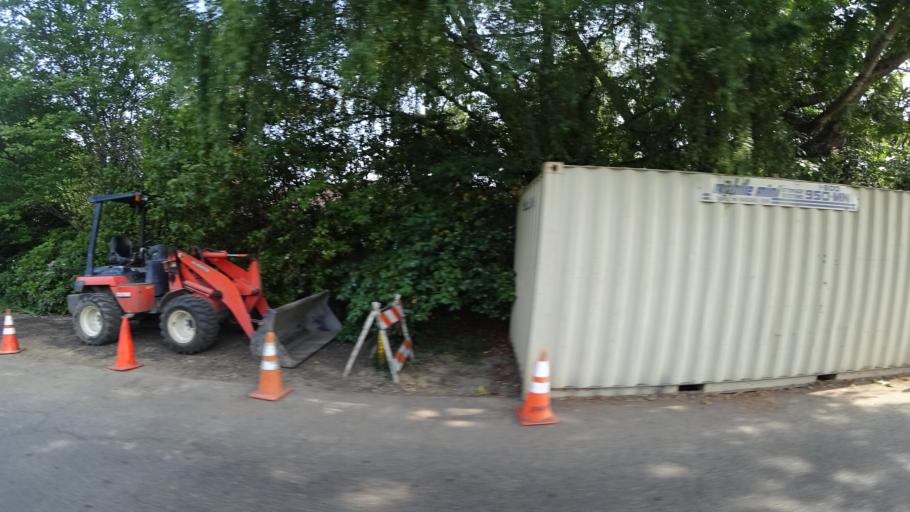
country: US
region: Oregon
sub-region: Washington County
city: Garden Home-Whitford
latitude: 45.4618
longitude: -122.7118
